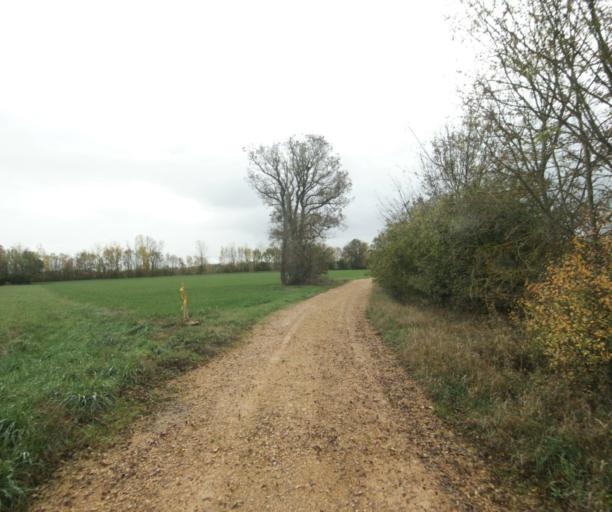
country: FR
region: Rhone-Alpes
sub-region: Departement de l'Ain
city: Pont-de-Vaux
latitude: 46.4570
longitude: 4.9026
